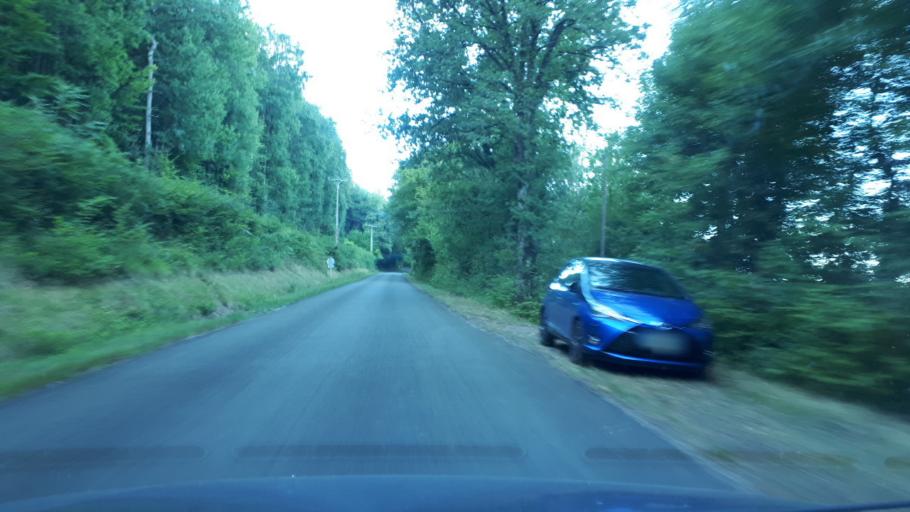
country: FR
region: Centre
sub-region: Departement du Loir-et-Cher
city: Villiers-sur-Loir
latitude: 47.7712
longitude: 0.9602
